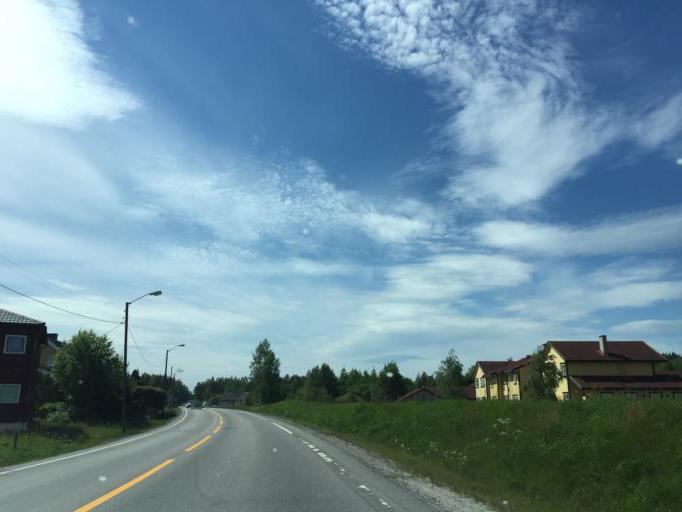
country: NO
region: Hedmark
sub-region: Sor-Odal
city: Skarnes
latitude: 60.2532
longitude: 11.6721
